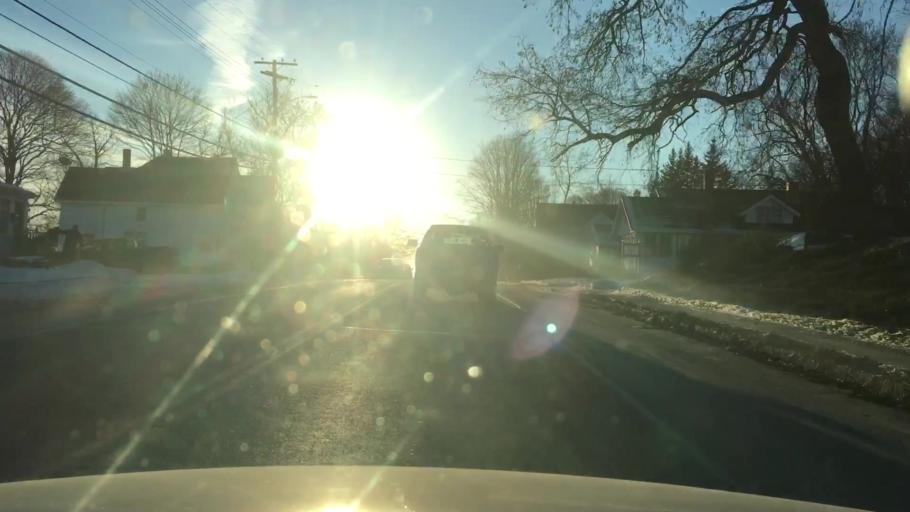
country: US
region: Maine
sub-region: Penobscot County
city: Brewer
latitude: 44.7998
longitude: -68.7560
